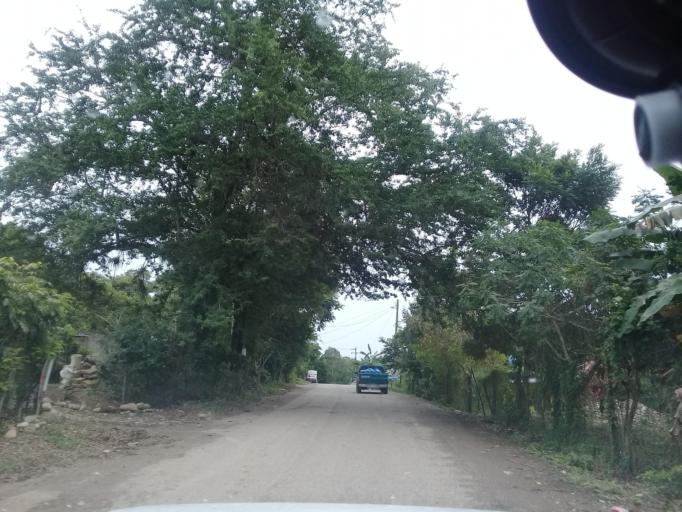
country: MX
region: Veracruz
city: Platon Sanchez
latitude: 21.2150
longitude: -98.3733
